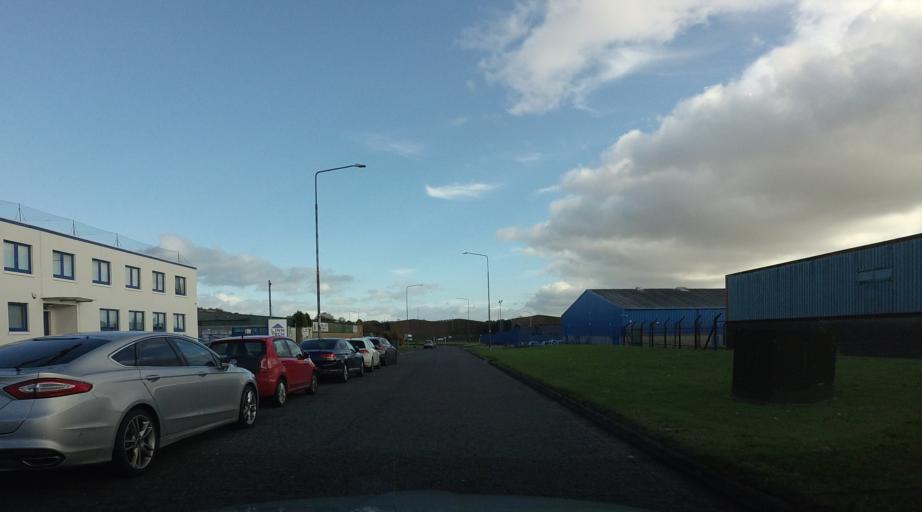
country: GB
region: Scotland
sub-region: West Lothian
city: Broxburn
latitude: 55.9387
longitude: -3.4501
